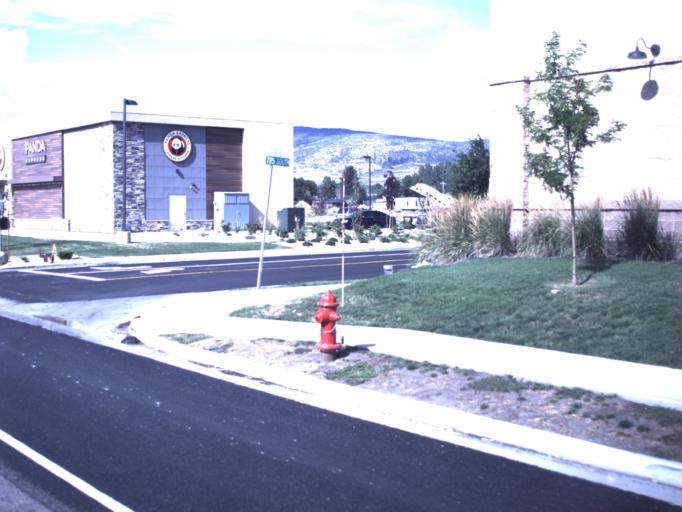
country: US
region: Utah
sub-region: Wasatch County
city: Heber
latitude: 40.4978
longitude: -111.4135
